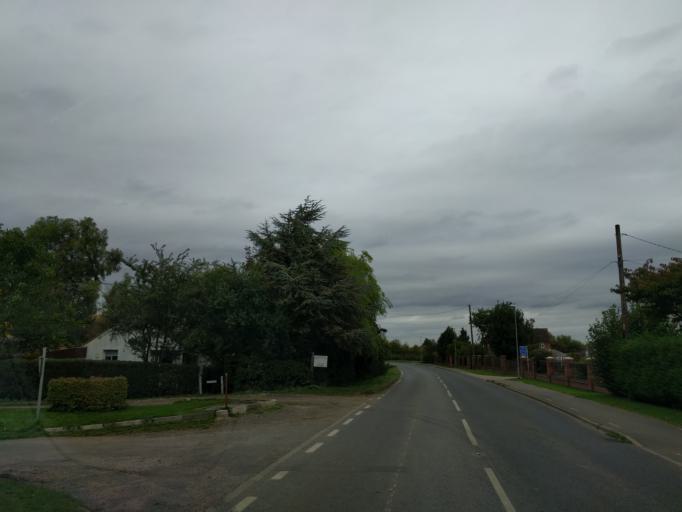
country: GB
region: England
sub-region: Cambridgeshire
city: Swavesey
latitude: 52.2978
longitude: 0.0507
